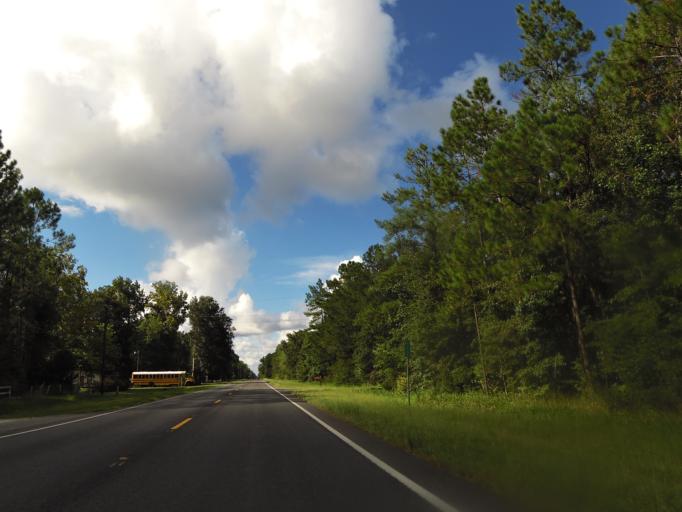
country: US
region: Georgia
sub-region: Camden County
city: Woodbine
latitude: 30.9130
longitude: -81.7125
